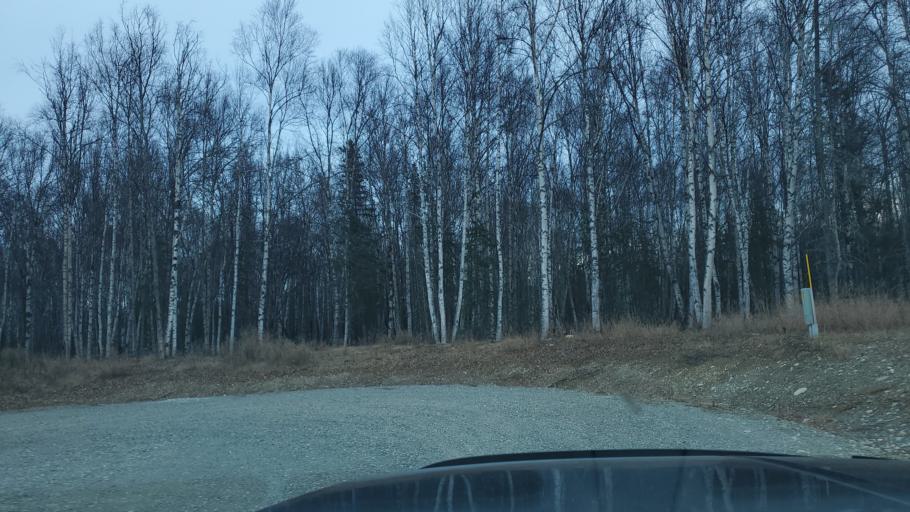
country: US
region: Alaska
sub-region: Matanuska-Susitna Borough
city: Lakes
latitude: 61.6542
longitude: -149.2895
